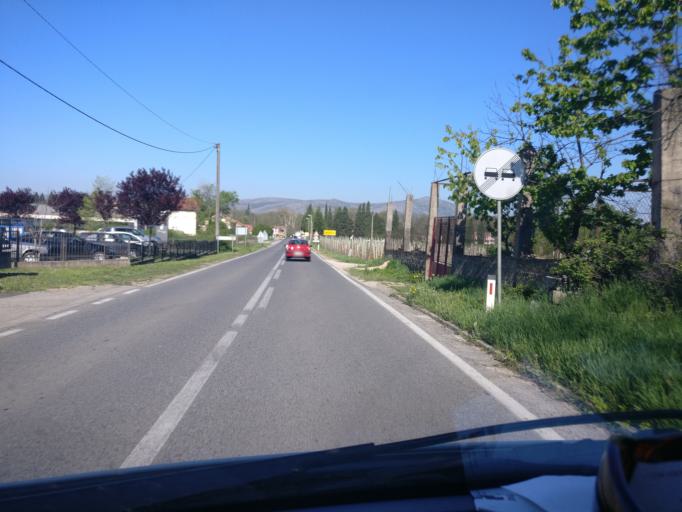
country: BA
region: Federation of Bosnia and Herzegovina
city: Tasovcici
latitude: 43.1367
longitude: 17.7850
